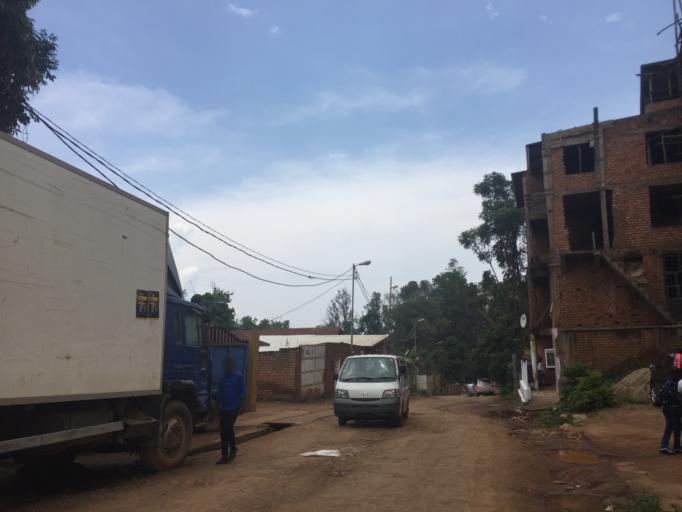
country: CD
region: South Kivu
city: Bukavu
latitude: -2.4859
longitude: 28.8586
